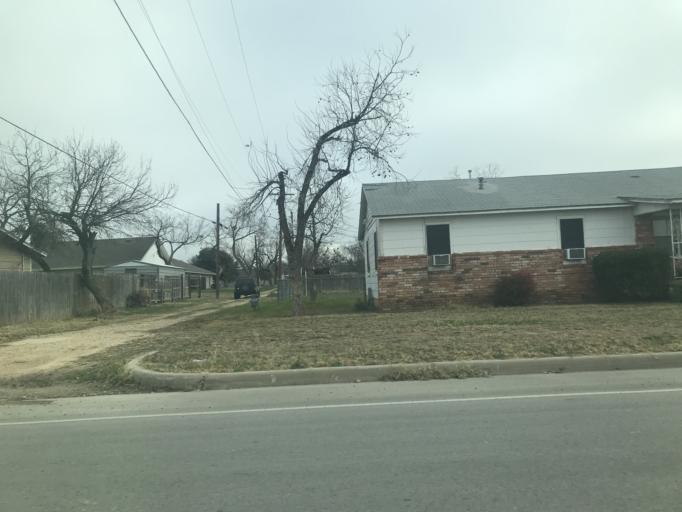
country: US
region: Texas
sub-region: Tom Green County
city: San Angelo
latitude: 31.4752
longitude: -100.4500
